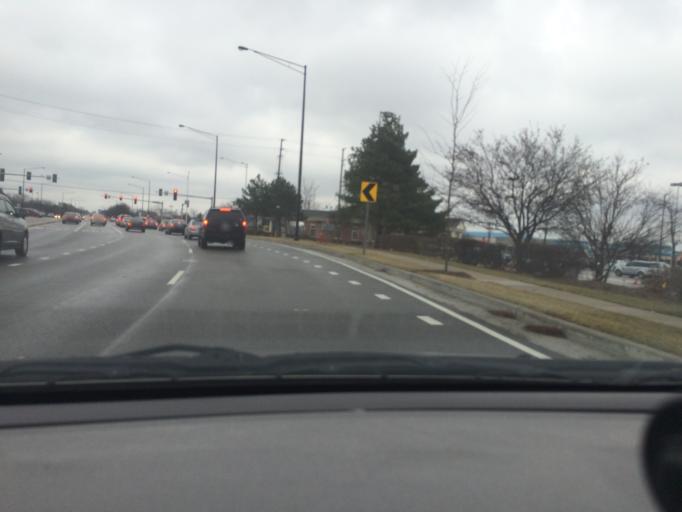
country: US
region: Illinois
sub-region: DuPage County
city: Hanover Park
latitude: 42.0247
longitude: -88.1463
